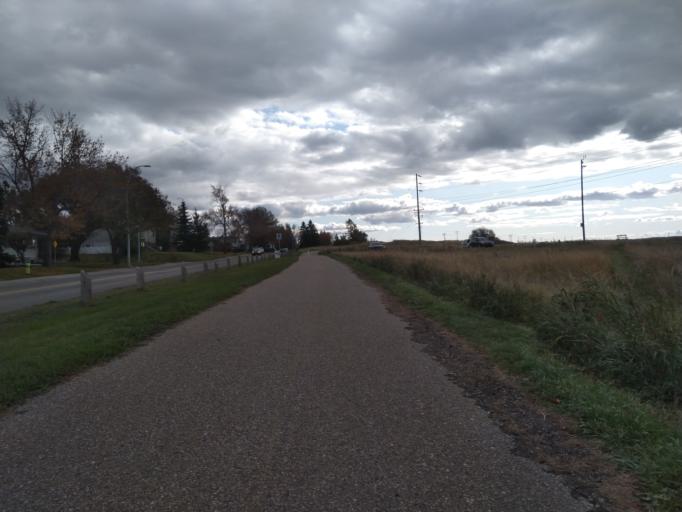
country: CA
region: Alberta
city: Calgary
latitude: 51.0345
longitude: -113.9953
